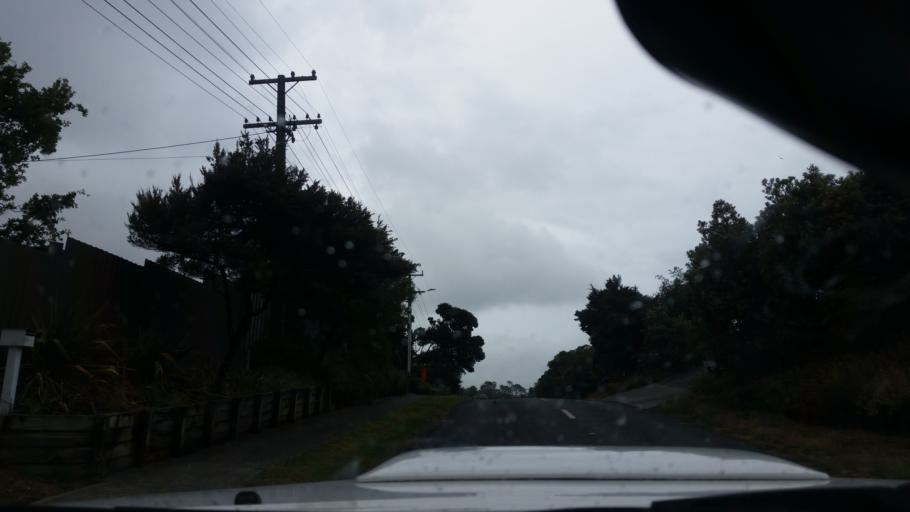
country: NZ
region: Auckland
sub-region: Auckland
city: Wellsford
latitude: -36.1040
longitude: 174.5910
